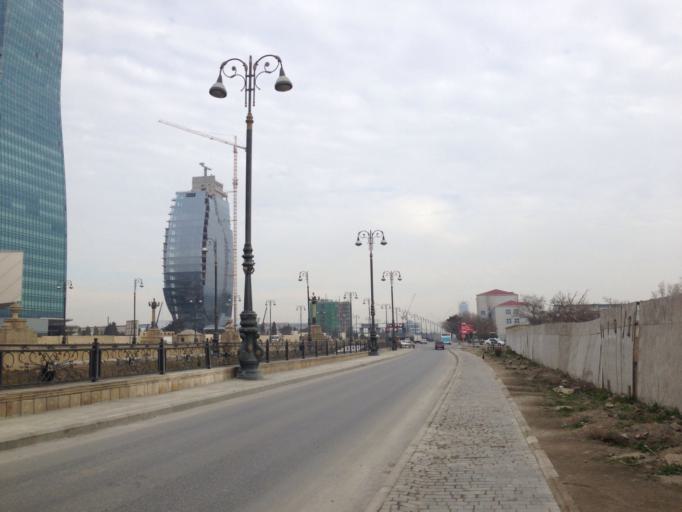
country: AZ
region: Baki
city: Baku
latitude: 40.4029
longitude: 49.8831
